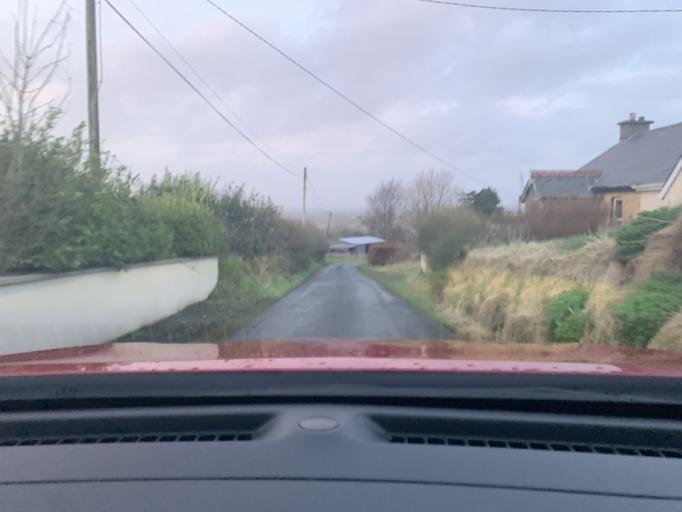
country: IE
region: Connaught
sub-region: Sligo
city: Ballymote
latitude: 54.0682
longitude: -8.3959
